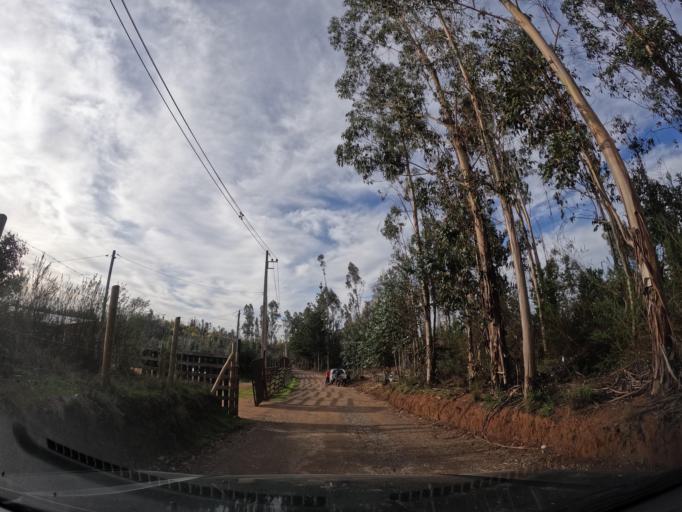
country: CL
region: Biobio
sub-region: Provincia de Concepcion
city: Chiguayante
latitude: -37.0296
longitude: -72.9055
